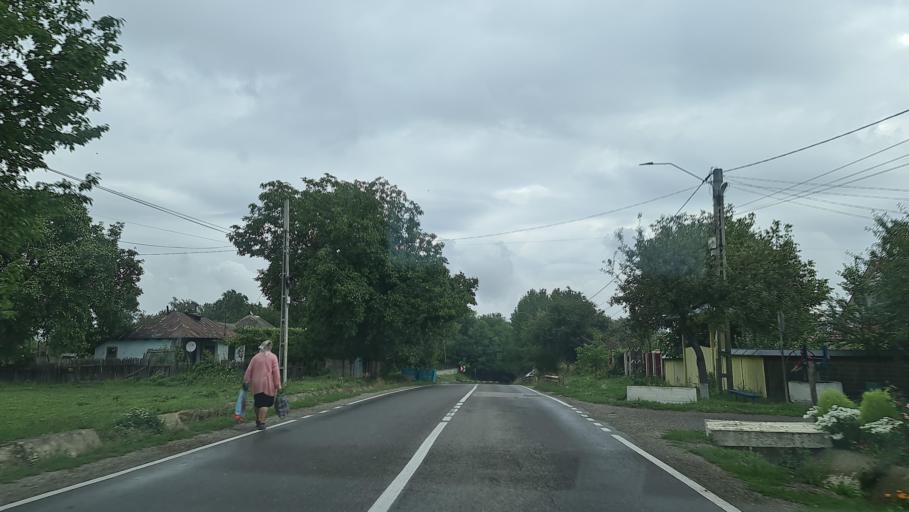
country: RO
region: Neamt
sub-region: Comuna Borlesti
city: Borlesti
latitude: 46.7699
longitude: 26.4847
